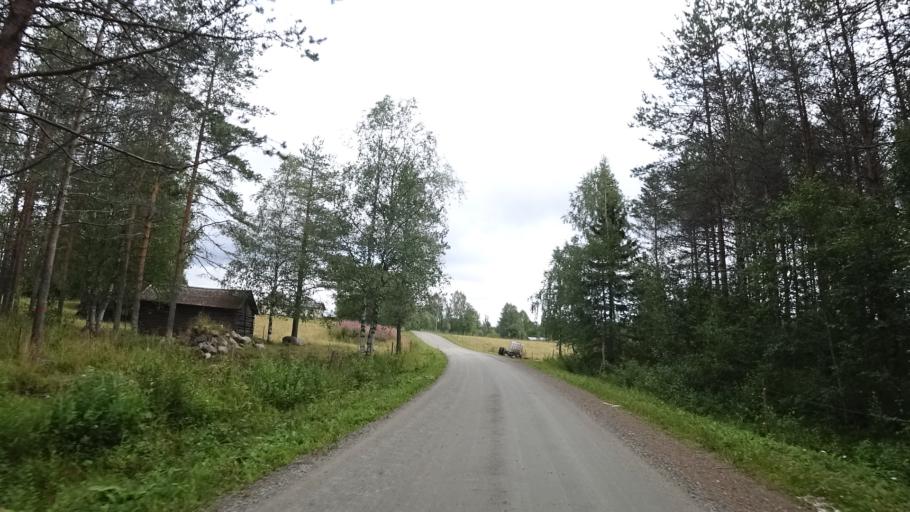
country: FI
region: North Karelia
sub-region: Joensuu
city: Ilomantsi
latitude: 62.9333
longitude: 31.2914
